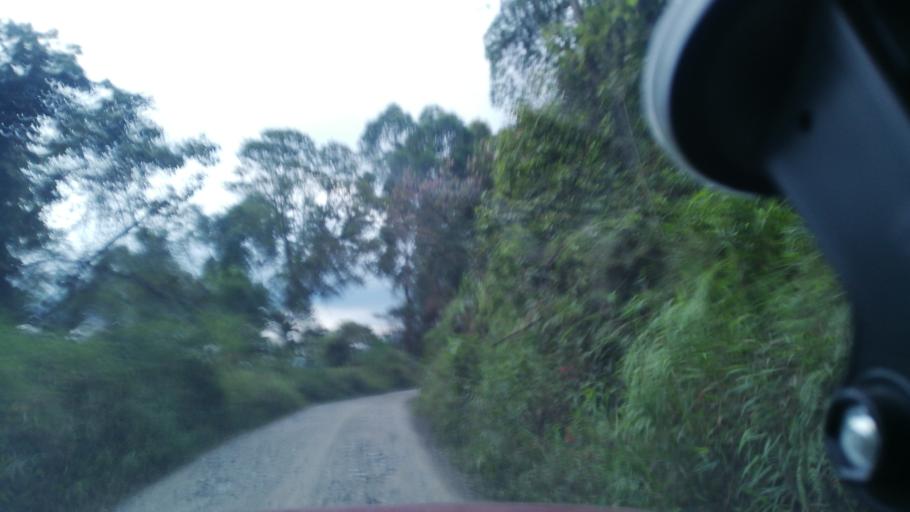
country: CO
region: Cundinamarca
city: Pacho
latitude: 5.1624
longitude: -74.2292
